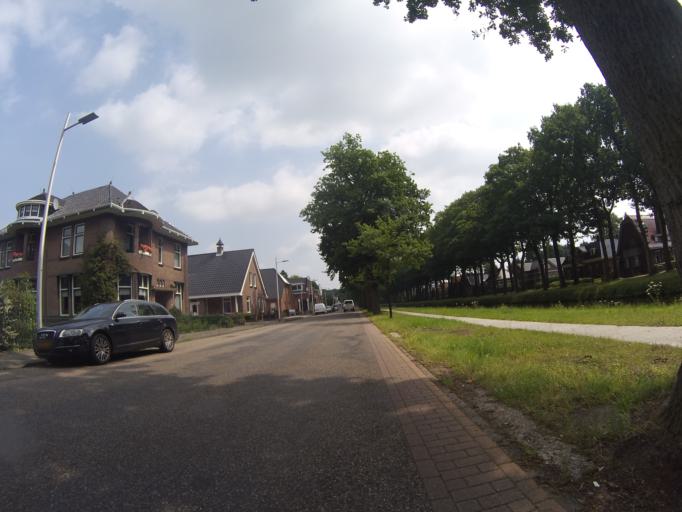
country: NL
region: Drenthe
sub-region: Gemeente Emmen
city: Emmer-Compascuum
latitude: 52.8739
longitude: 7.0667
